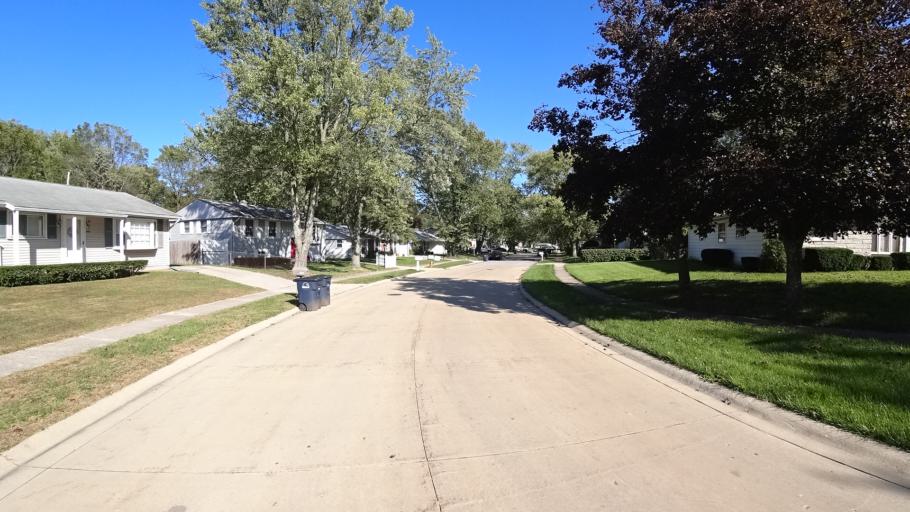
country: US
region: Indiana
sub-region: LaPorte County
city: Michigan City
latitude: 41.6919
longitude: -86.9067
